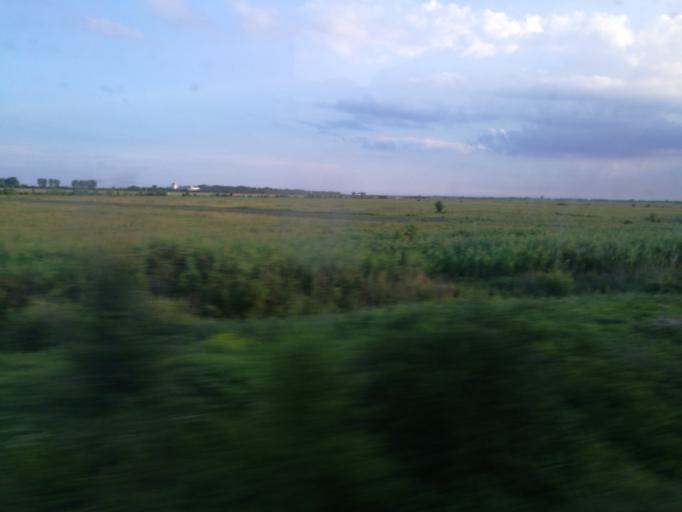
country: RO
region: Dambovita
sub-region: Comuna Contesti
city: Contesti
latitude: 44.6601
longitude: 25.6193
